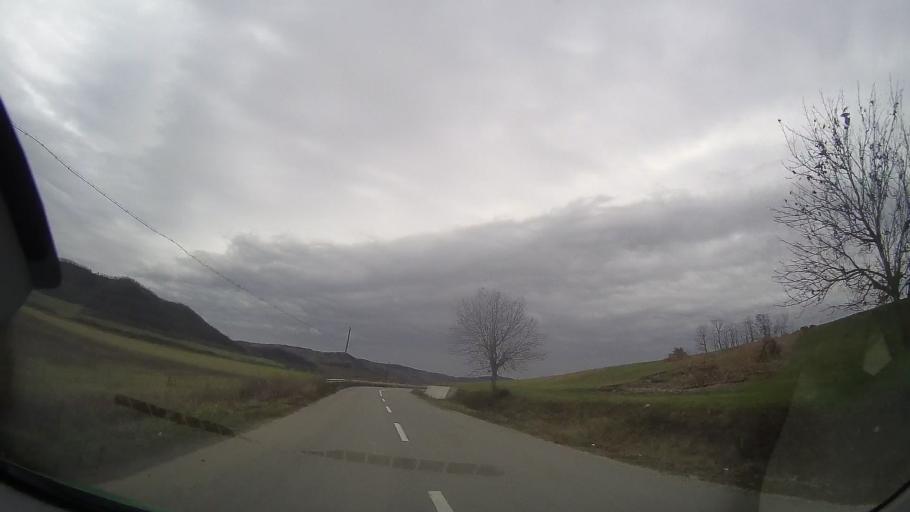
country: RO
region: Bistrita-Nasaud
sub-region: Comuna Milas
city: Milas
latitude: 46.7961
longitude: 24.4218
